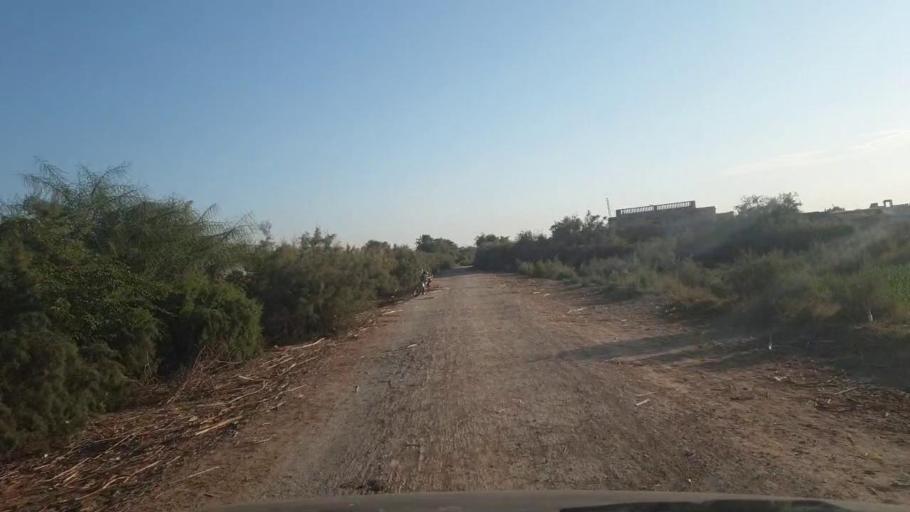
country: PK
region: Sindh
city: Sinjhoro
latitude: 26.0476
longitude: 68.8692
